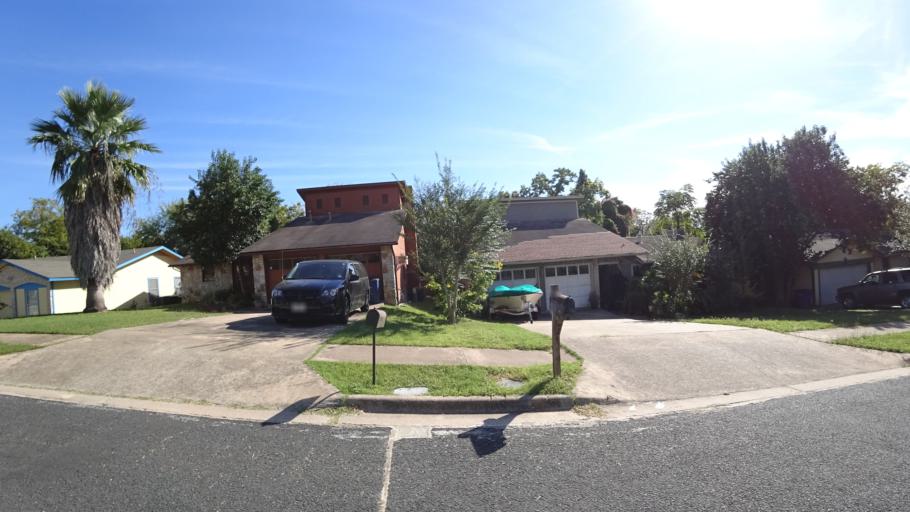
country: US
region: Texas
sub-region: Travis County
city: Onion Creek
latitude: 30.1927
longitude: -97.7433
